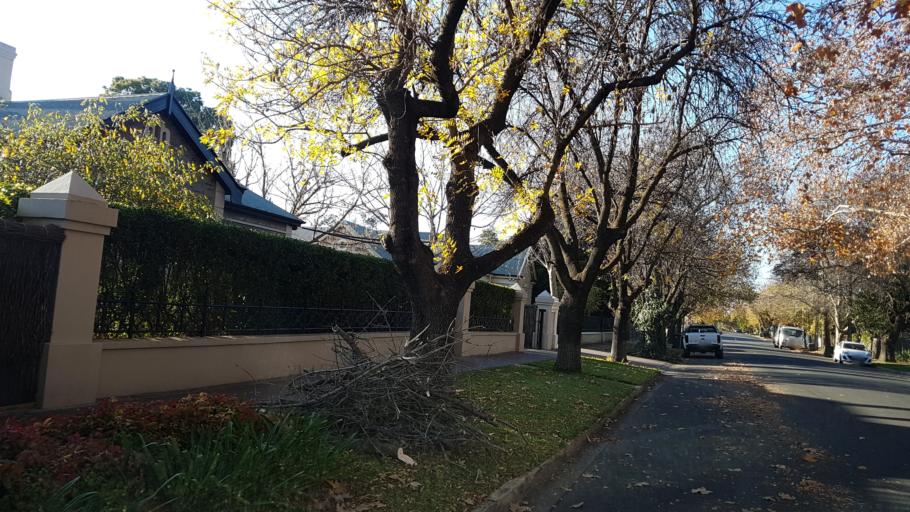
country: AU
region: South Australia
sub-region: Norwood Payneham St Peters
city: Royston Park
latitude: -34.9060
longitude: 138.6228
